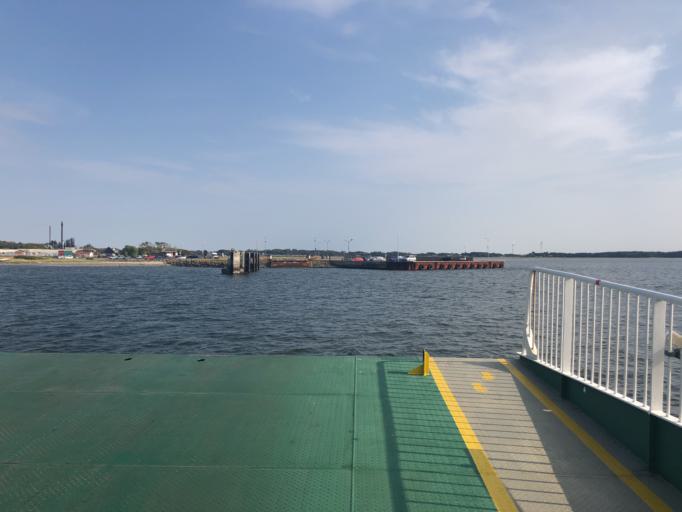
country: DK
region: North Denmark
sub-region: Morso Kommune
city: Nykobing Mors
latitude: 56.8014
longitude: 9.0246
